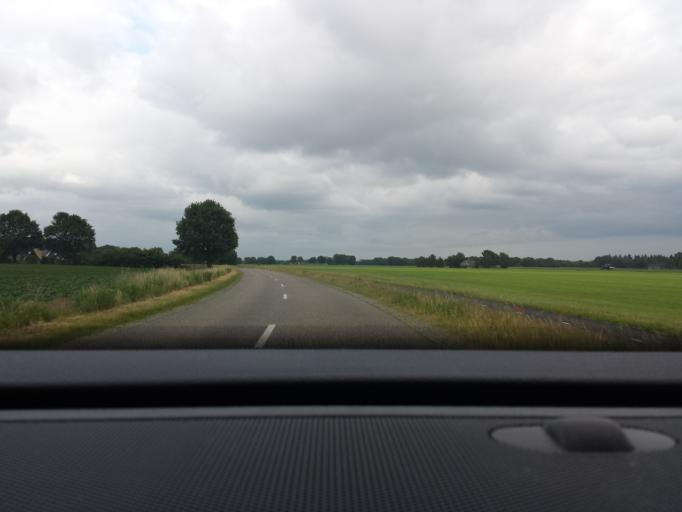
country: NL
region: Gelderland
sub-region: Gemeente Bronckhorst
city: Hengelo
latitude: 52.0310
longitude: 6.3182
